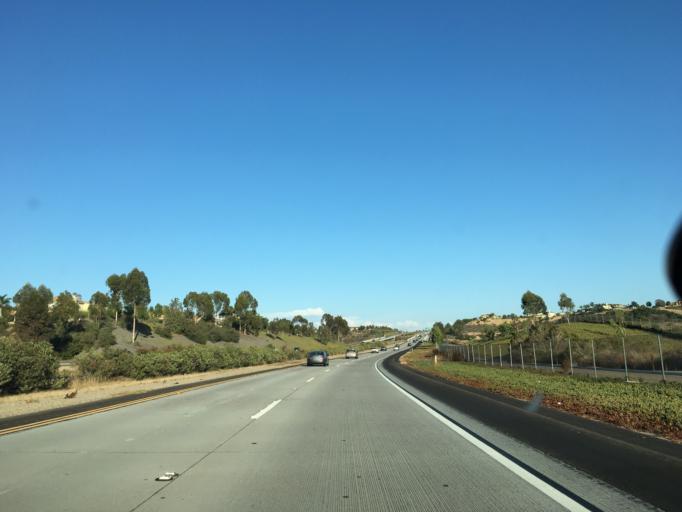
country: US
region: California
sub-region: San Diego County
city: Fairbanks Ranch
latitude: 32.9663
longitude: -117.1686
